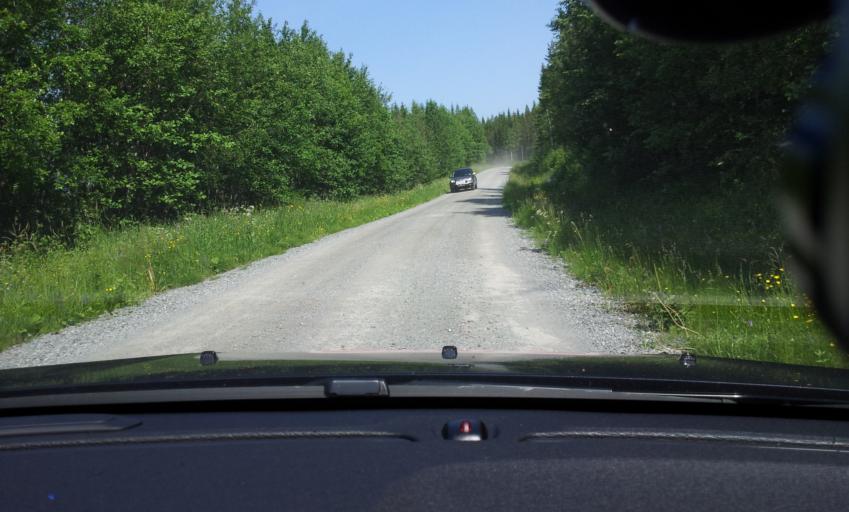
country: SE
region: Jaemtland
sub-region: Bergs Kommun
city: Hoverberg
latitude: 62.7857
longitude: 14.4545
